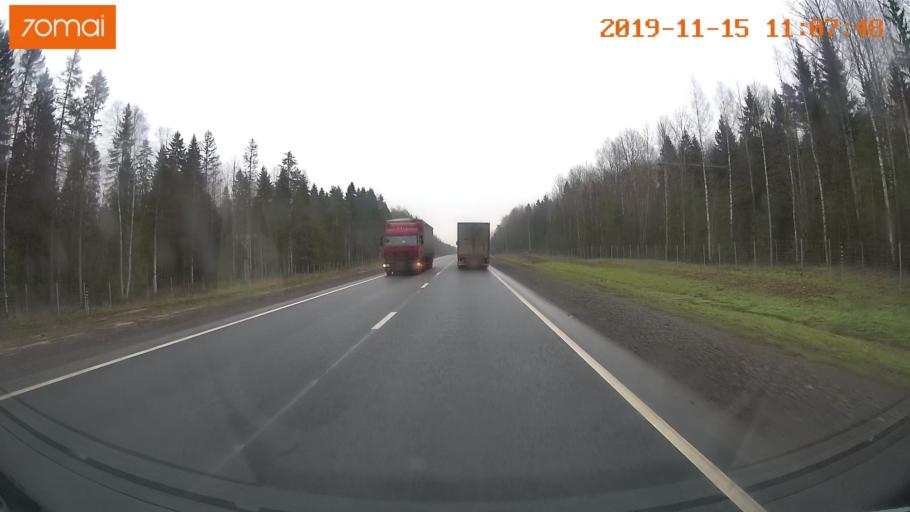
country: RU
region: Vologda
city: Chebsara
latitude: 59.1197
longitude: 39.0593
